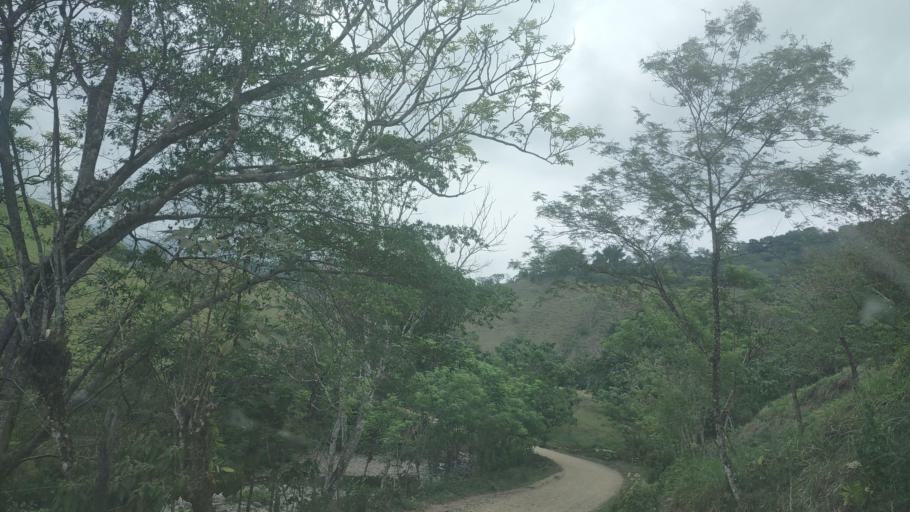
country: MX
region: Tabasco
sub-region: Huimanguillo
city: Francisco Rueda
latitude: 17.4394
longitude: -94.0296
